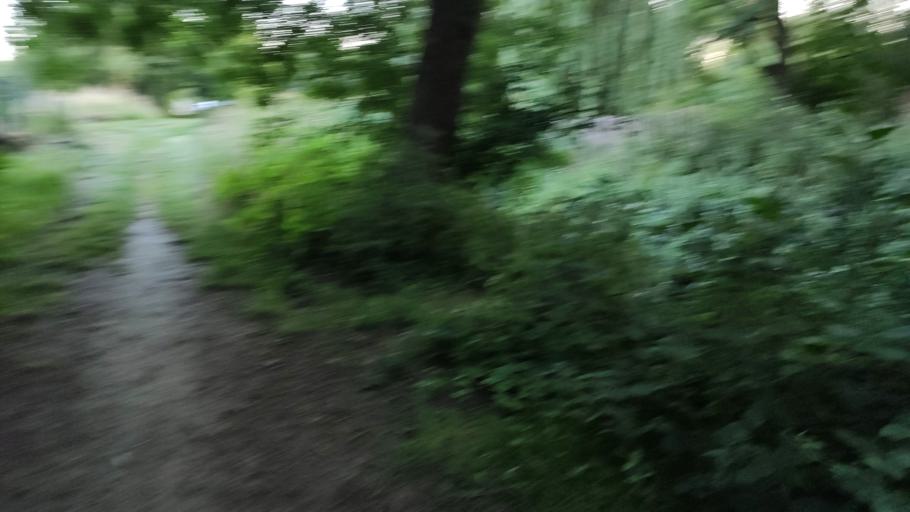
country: BE
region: Flanders
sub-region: Provincie Vlaams-Brabant
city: Hoegaarden
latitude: 50.7603
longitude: 4.8874
